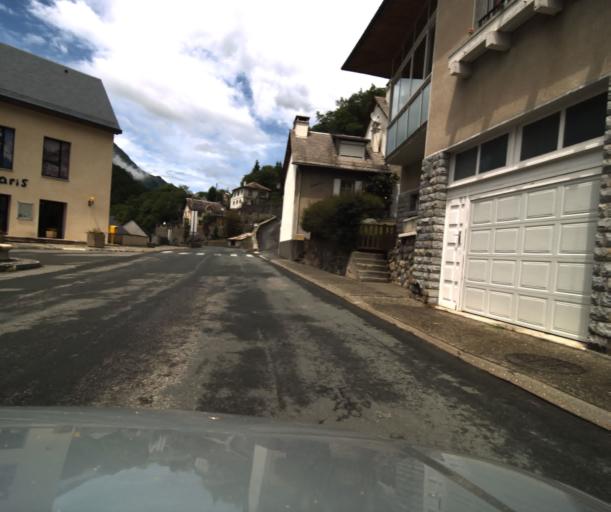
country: FR
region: Midi-Pyrenees
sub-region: Departement des Hautes-Pyrenees
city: Luz-Saint-Sauveur
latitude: 42.7888
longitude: 0.0195
